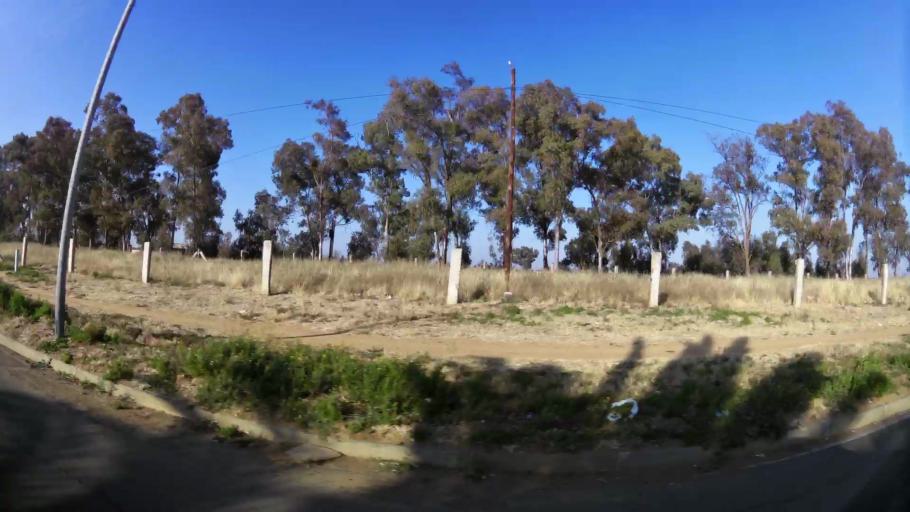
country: ZA
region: Orange Free State
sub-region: Mangaung Metropolitan Municipality
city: Bloemfontein
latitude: -29.1321
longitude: 26.2573
